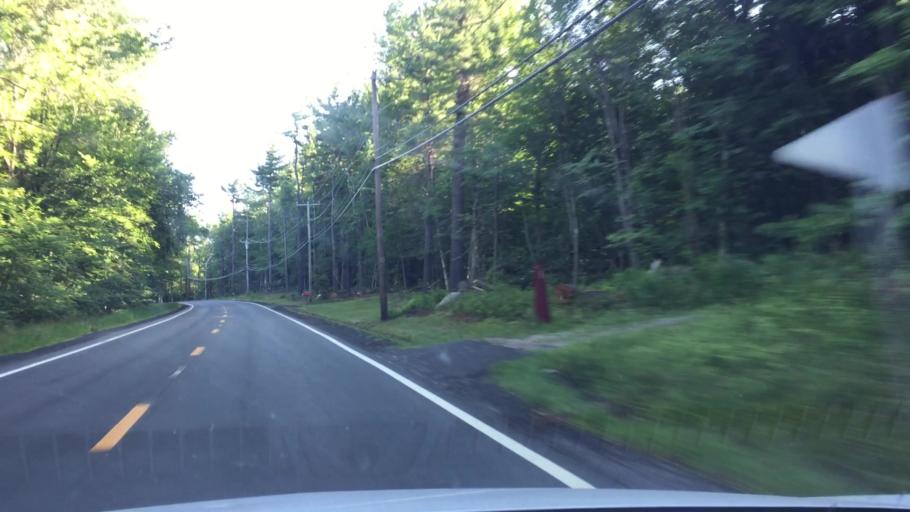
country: US
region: Massachusetts
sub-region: Berkshire County
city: Becket
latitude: 42.2945
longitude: -73.0577
